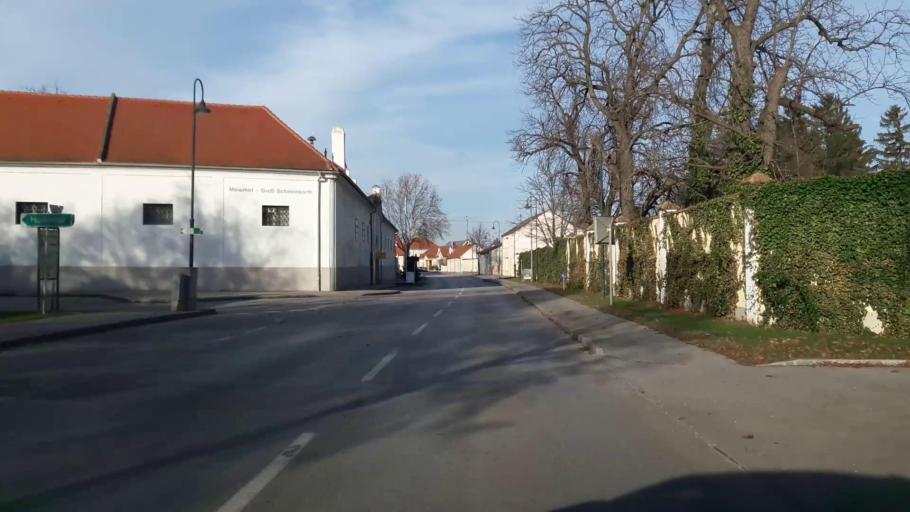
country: AT
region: Lower Austria
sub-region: Politischer Bezirk Ganserndorf
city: Gross-Schweinbarth
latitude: 48.4125
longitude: 16.6352
